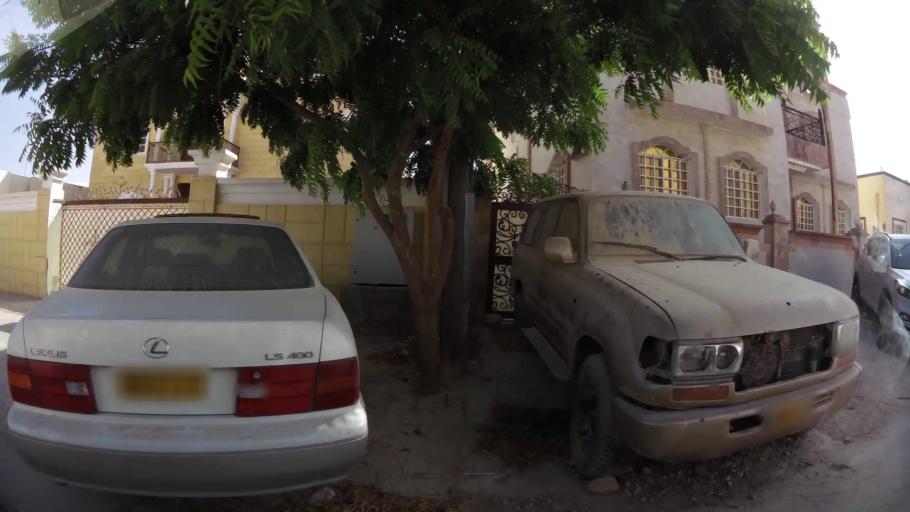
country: OM
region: Zufar
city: Salalah
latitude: 17.0074
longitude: 54.0016
